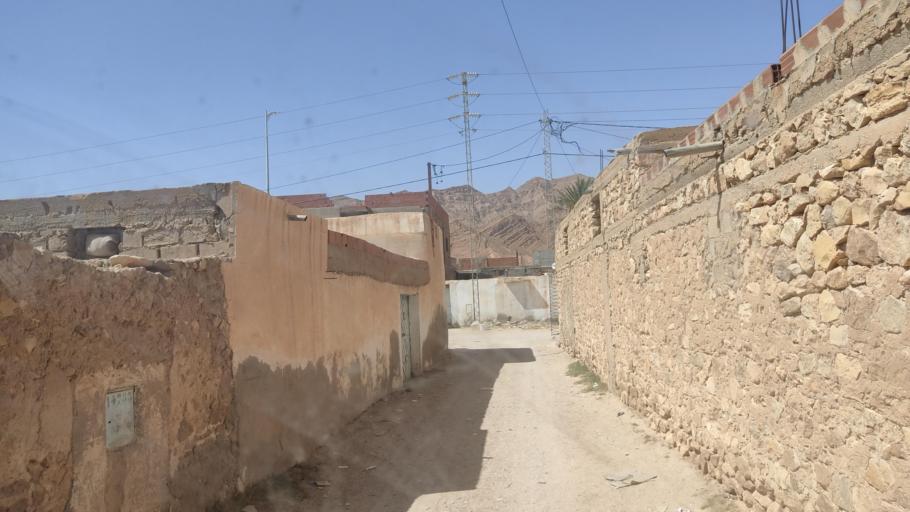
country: TN
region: Gafsa
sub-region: Gafsa Municipality
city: Gafsa
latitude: 34.3366
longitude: 8.9199
